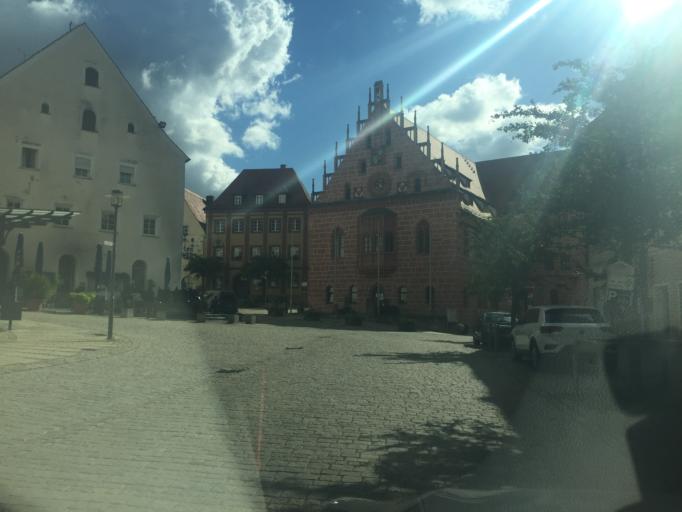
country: DE
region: Bavaria
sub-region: Upper Palatinate
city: Sulzbach-Rosenberg
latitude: 49.5052
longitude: 11.7387
